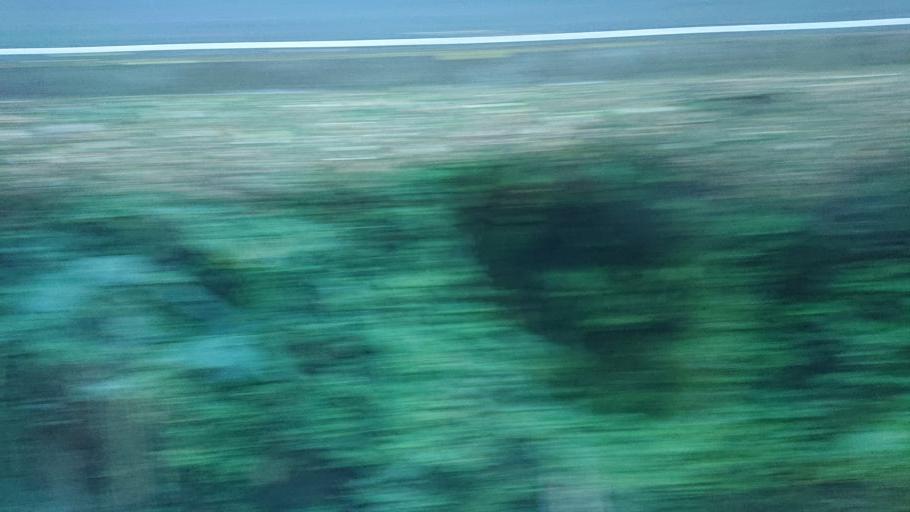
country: TW
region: Taiwan
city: Lugu
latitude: 23.4902
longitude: 120.7586
